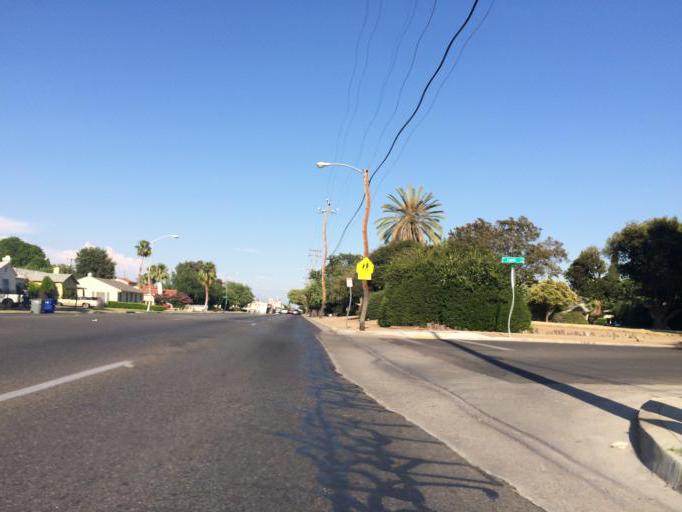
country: US
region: California
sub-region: Fresno County
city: Fresno
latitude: 36.7431
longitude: -119.7581
